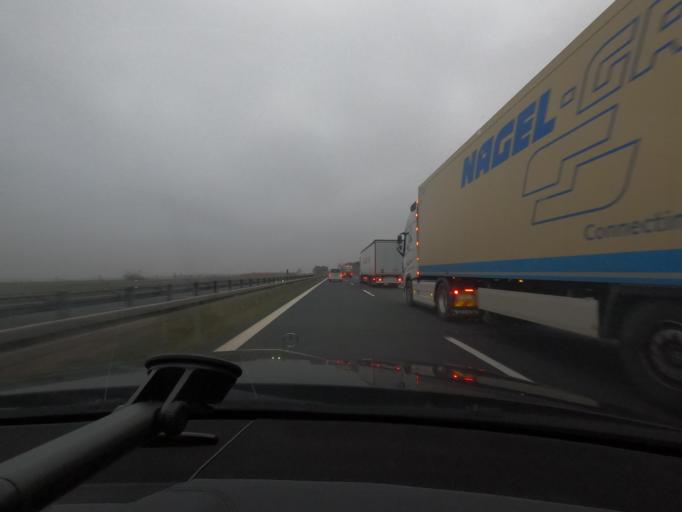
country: DE
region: Brandenburg
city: Gross Kreutz
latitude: 52.3484
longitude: 12.8134
